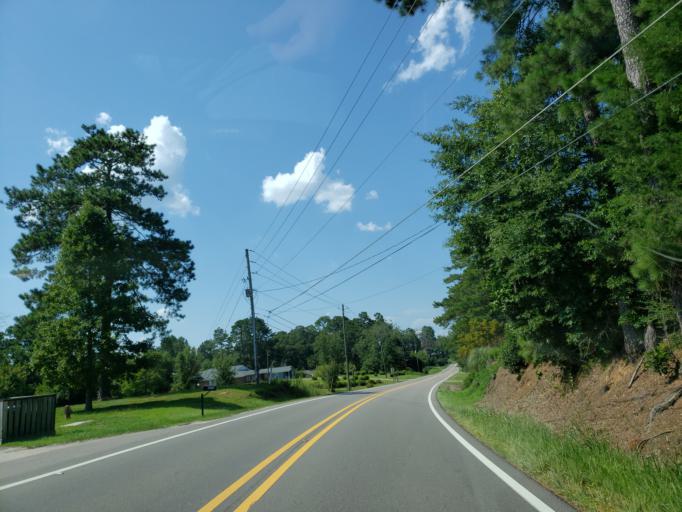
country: US
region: Mississippi
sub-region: Lamar County
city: Sumrall
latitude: 31.4080
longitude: -89.5457
